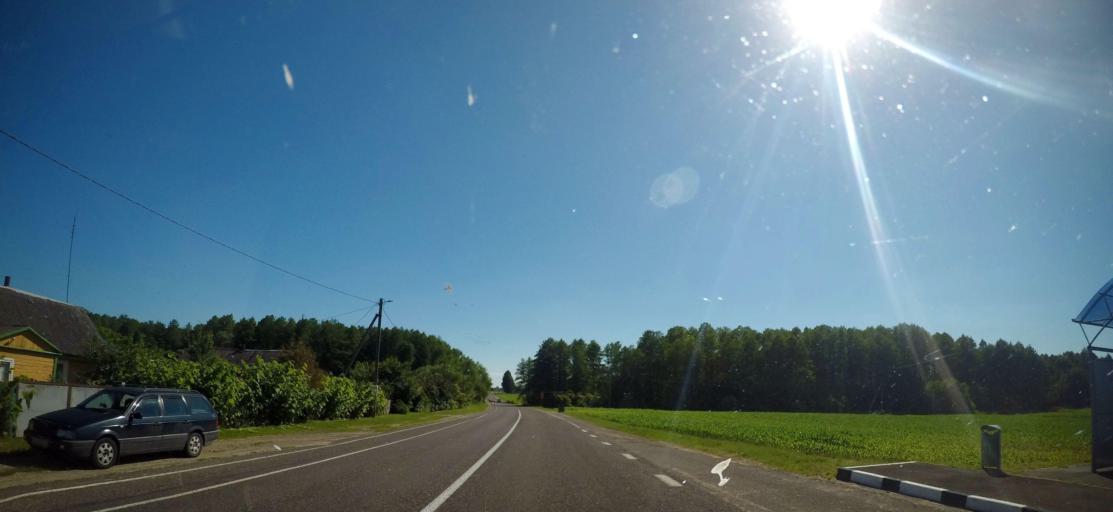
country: BY
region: Grodnenskaya
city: Vyalikaya Byerastavitsa
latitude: 53.1770
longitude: 24.0003
